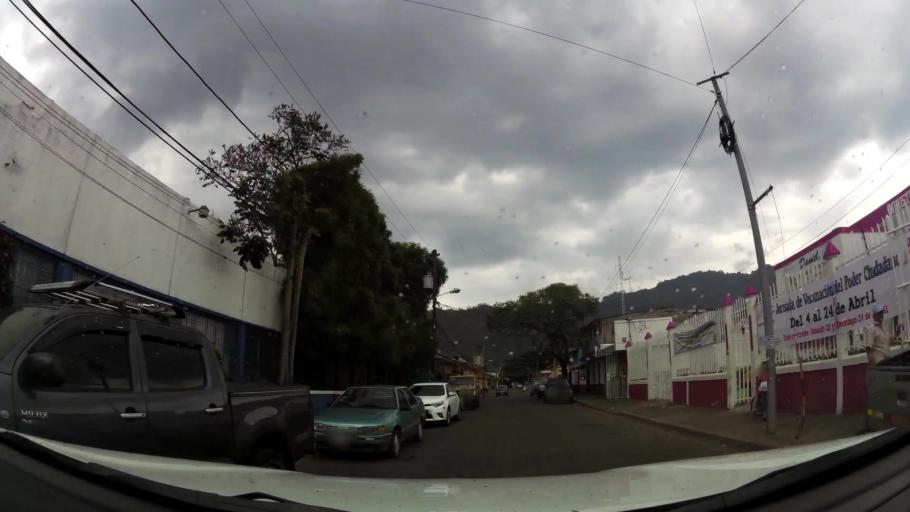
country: NI
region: Jinotega
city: Jinotega
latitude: 13.0898
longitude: -86.0018
